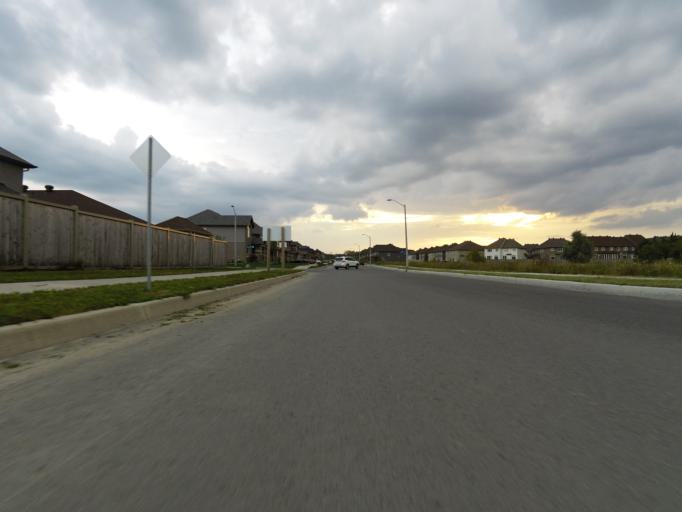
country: CA
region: Ontario
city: Bells Corners
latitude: 45.2745
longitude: -75.7789
